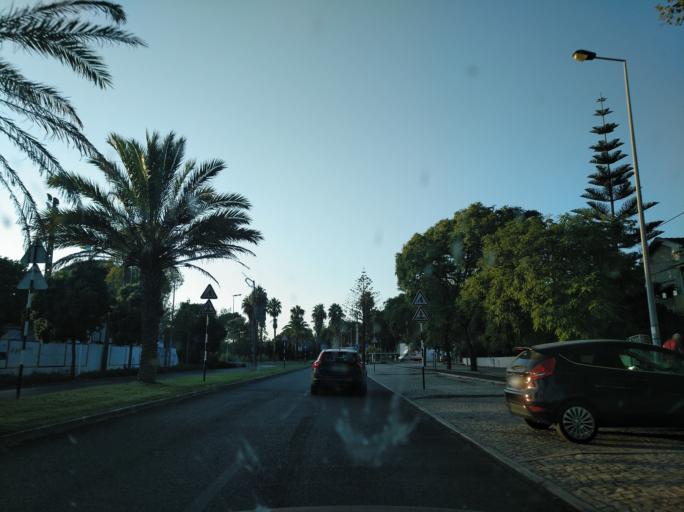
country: PT
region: Setubal
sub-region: Almada
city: Trafaria
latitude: 38.6632
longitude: -9.2432
